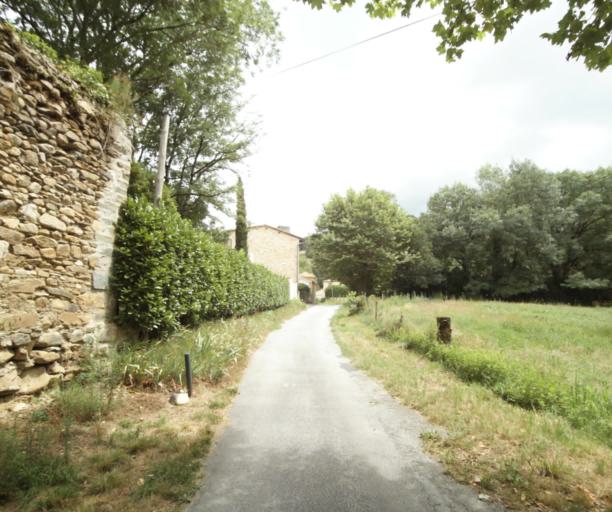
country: FR
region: Midi-Pyrenees
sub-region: Departement du Tarn
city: Soreze
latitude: 43.4504
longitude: 2.0710
